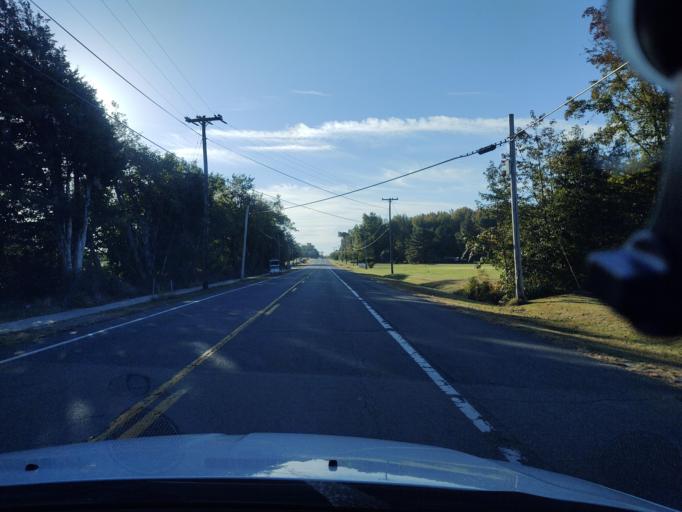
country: US
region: Maryland
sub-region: Queen Anne's County
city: Kingstown
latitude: 39.2383
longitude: -75.9193
